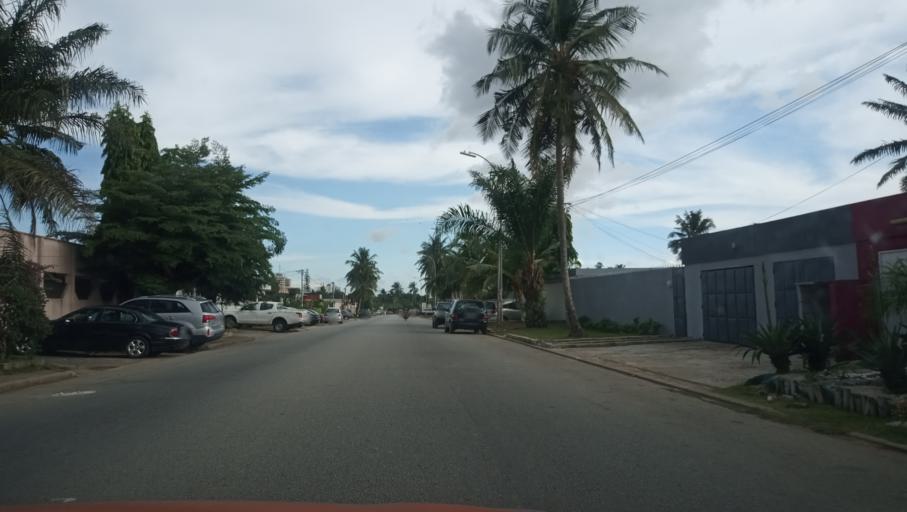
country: CI
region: Lagunes
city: Abidjan
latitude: 5.3475
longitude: -3.9800
